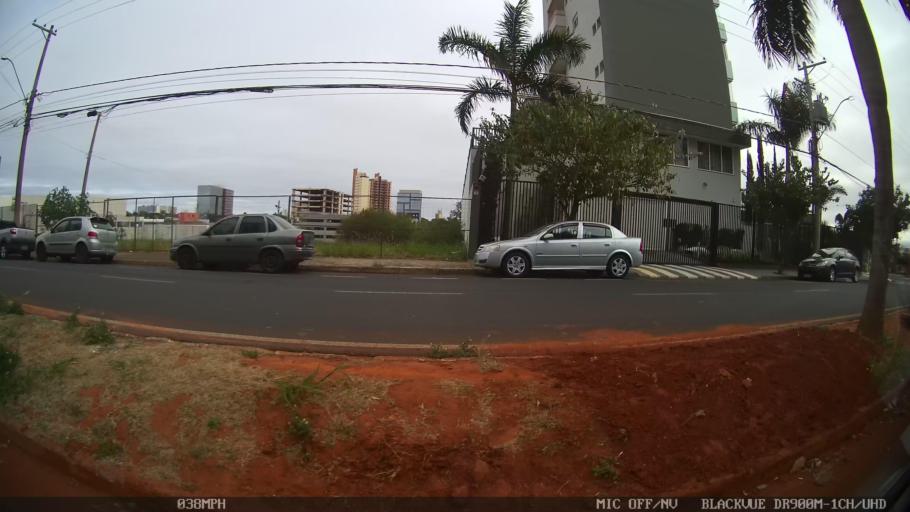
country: BR
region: Sao Paulo
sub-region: Sao Jose Do Rio Preto
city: Sao Jose do Rio Preto
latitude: -20.8271
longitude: -49.3840
